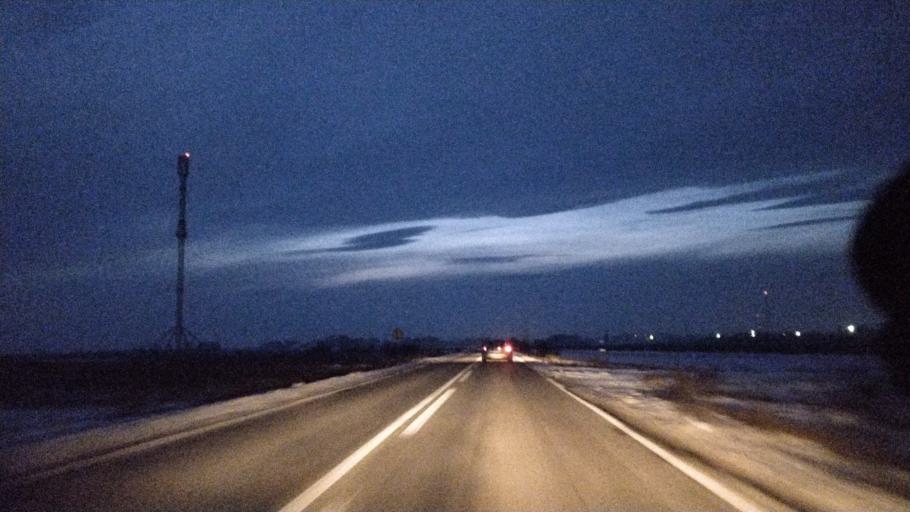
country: RO
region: Vrancea
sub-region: Comuna Milcovul
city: Milcovul
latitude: 45.6771
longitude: 27.2486
